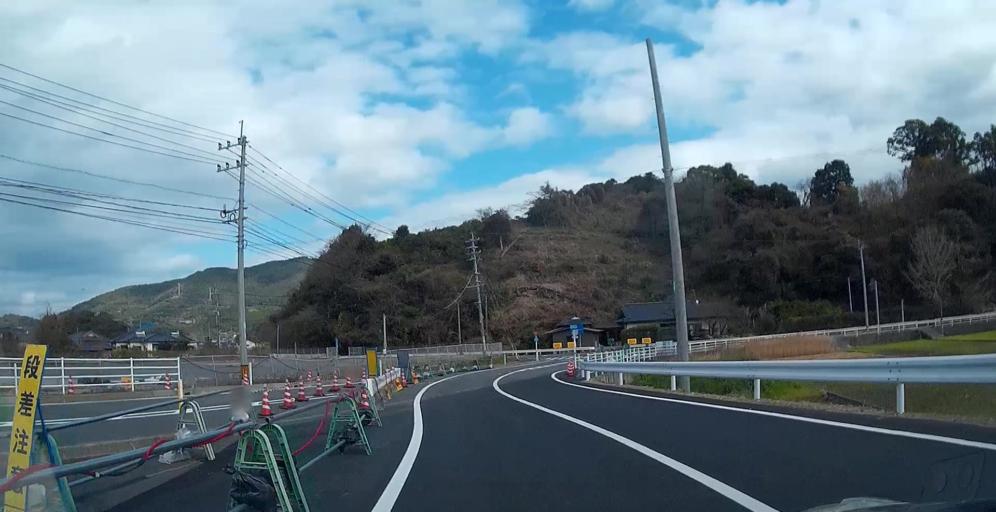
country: JP
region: Kumamoto
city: Minamata
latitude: 32.2276
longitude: 130.4355
